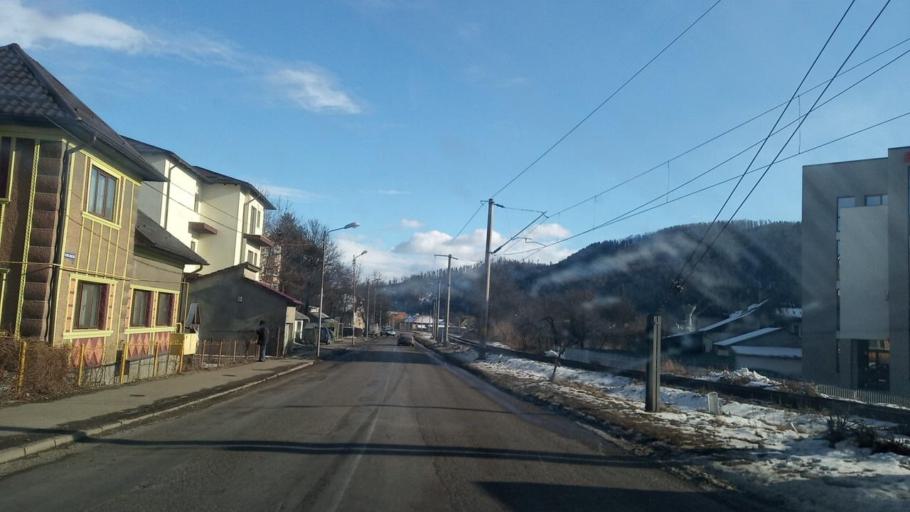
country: RO
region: Suceava
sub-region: Oras Gura Humorului
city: Gura Humorului
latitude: 47.5531
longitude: 25.8898
